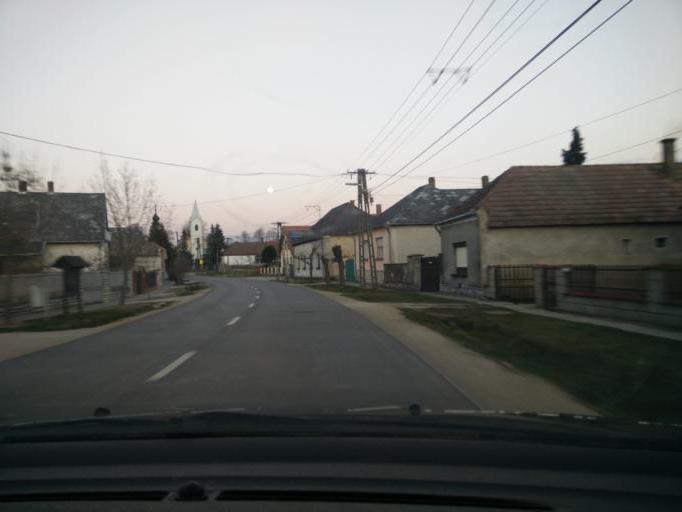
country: HU
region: Veszprem
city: Devecser
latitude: 47.0698
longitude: 17.3660
